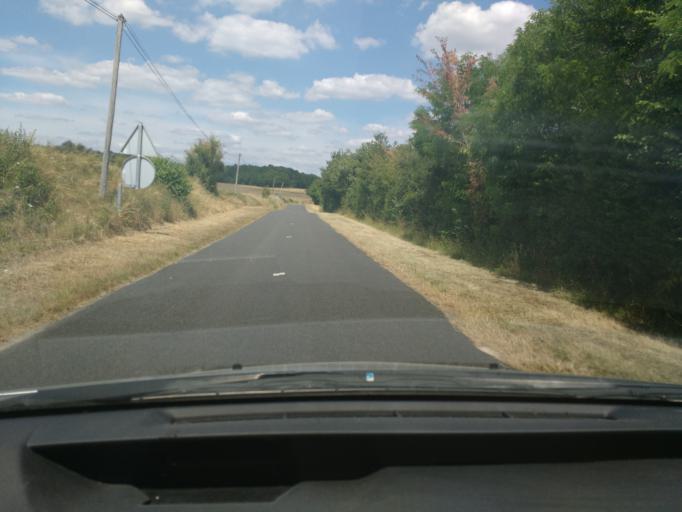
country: FR
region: Pays de la Loire
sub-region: Departement de Maine-et-Loire
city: Bauge-en-Anjou
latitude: 47.5439
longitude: -0.0886
